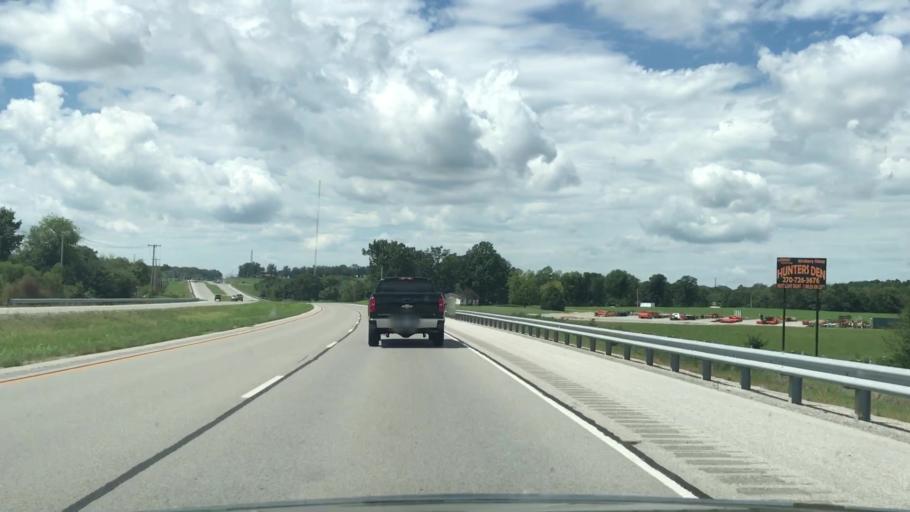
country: US
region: Kentucky
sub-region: Logan County
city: Russellville
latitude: 36.8676
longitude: -86.8964
